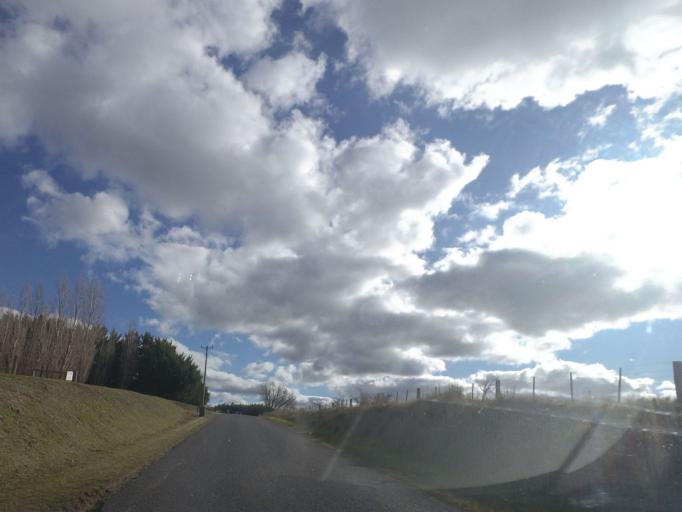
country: AU
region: Victoria
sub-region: Mount Alexander
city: Castlemaine
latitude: -37.2500
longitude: 144.3895
